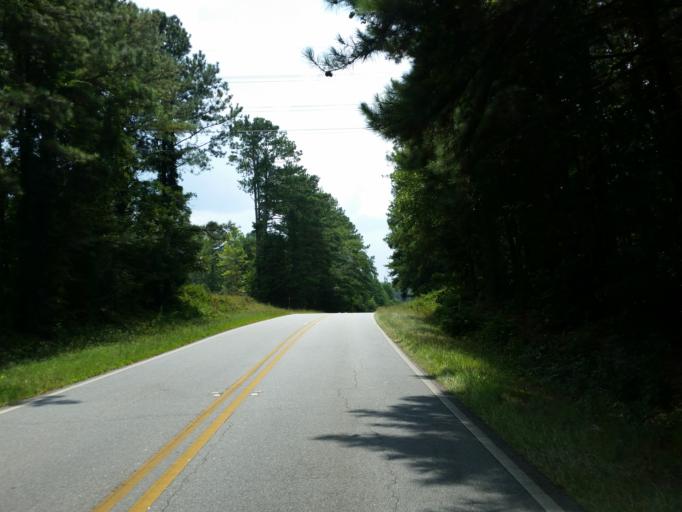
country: US
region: Georgia
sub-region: Butts County
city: Indian Springs
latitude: 33.1615
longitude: -84.0476
